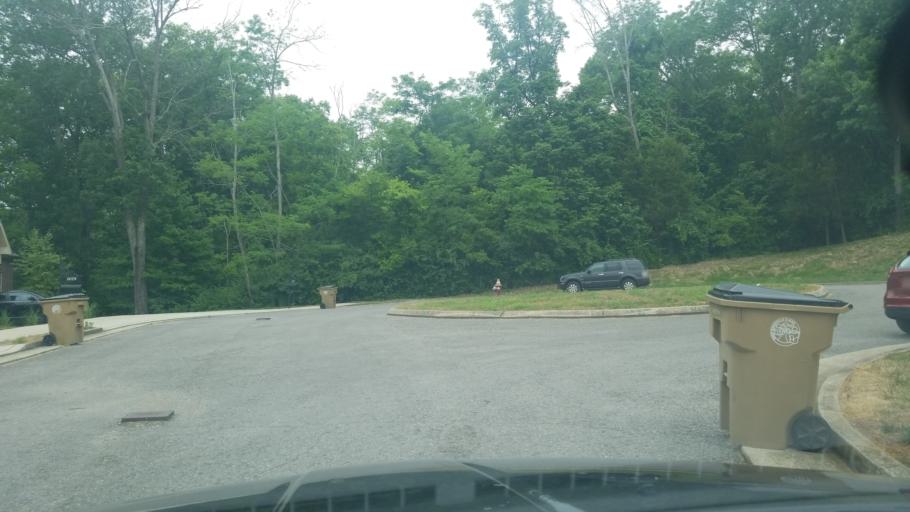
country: US
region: Tennessee
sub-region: Davidson County
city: Goodlettsville
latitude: 36.2543
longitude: -86.7412
